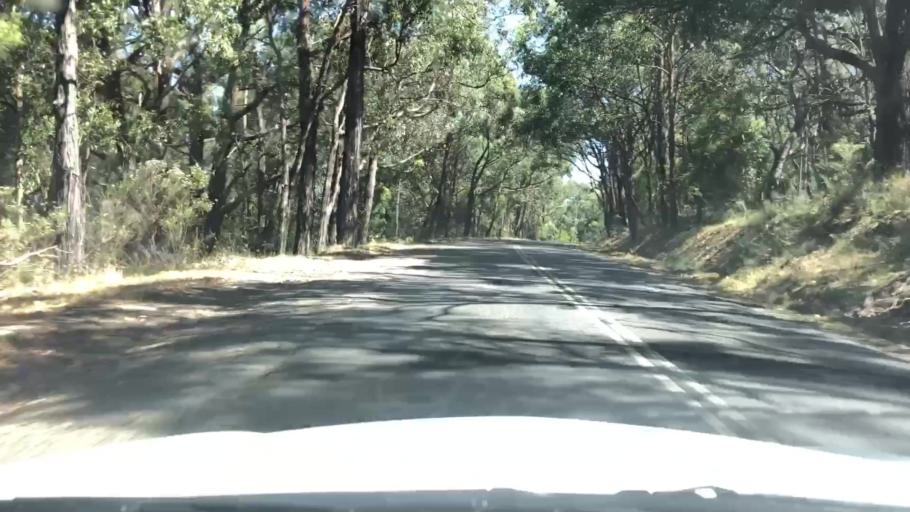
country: AU
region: Victoria
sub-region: Yarra Ranges
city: Macclesfield
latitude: -37.8779
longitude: 145.4777
